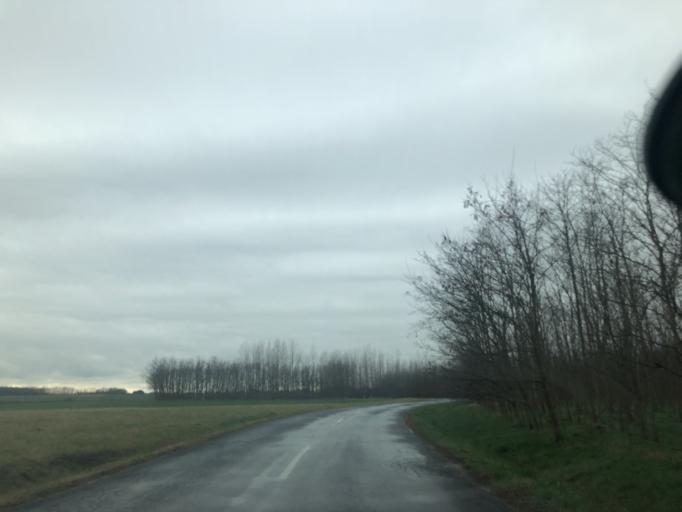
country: HU
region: Gyor-Moson-Sopron
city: Fertoszentmiklos
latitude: 47.6066
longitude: 16.9361
